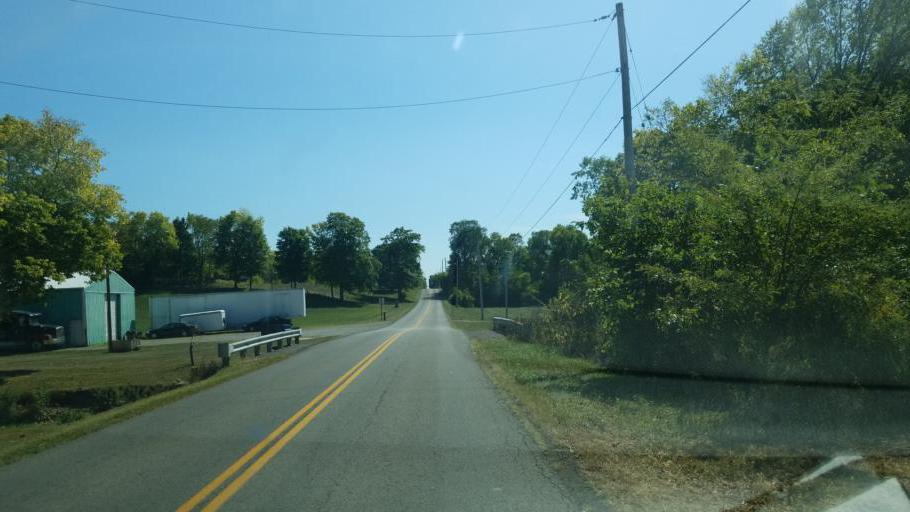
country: US
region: Ohio
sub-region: Logan County
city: Bellefontaine
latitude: 40.3756
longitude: -83.7717
